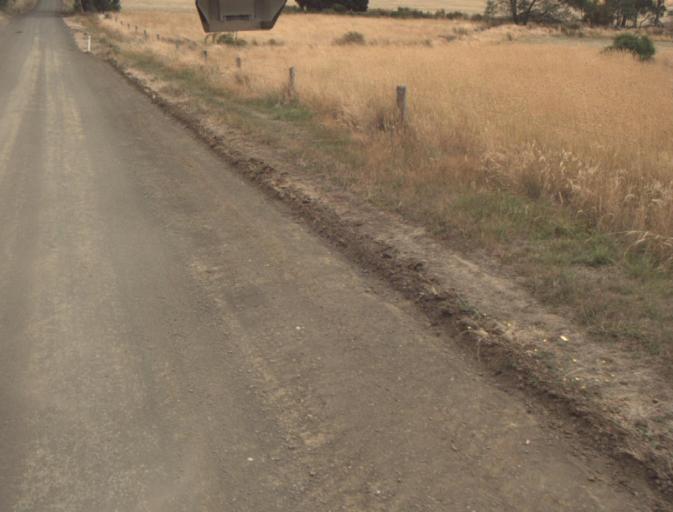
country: AU
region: Tasmania
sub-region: Northern Midlands
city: Evandale
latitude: -41.5229
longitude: 147.3670
